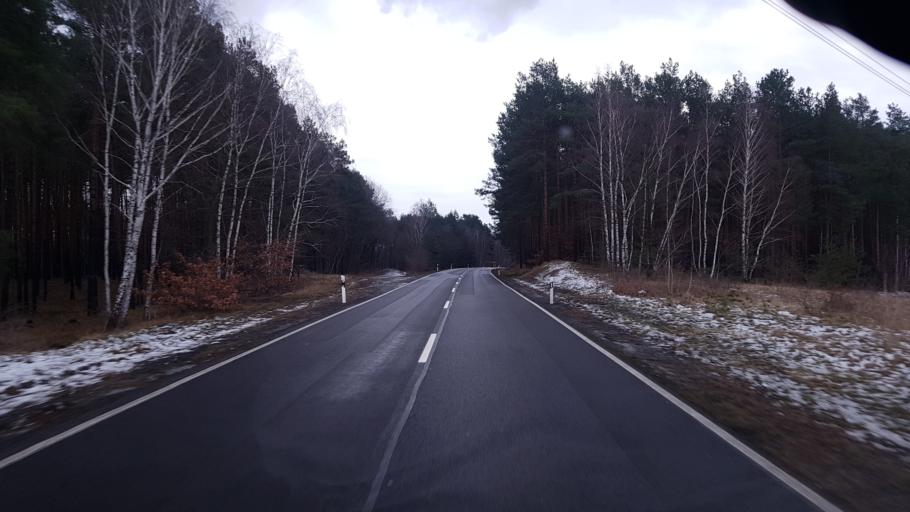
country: DE
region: Brandenburg
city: Janschwalde
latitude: 51.8424
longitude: 14.4627
